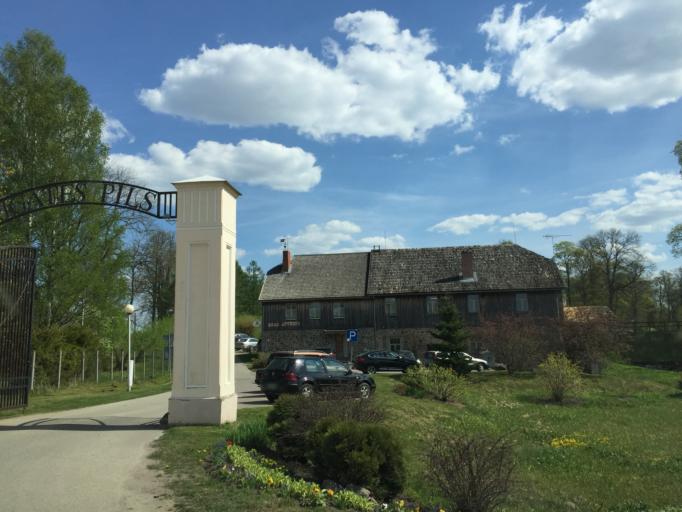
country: LV
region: Limbazu Rajons
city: Limbazi
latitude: 57.3813
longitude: 24.6836
